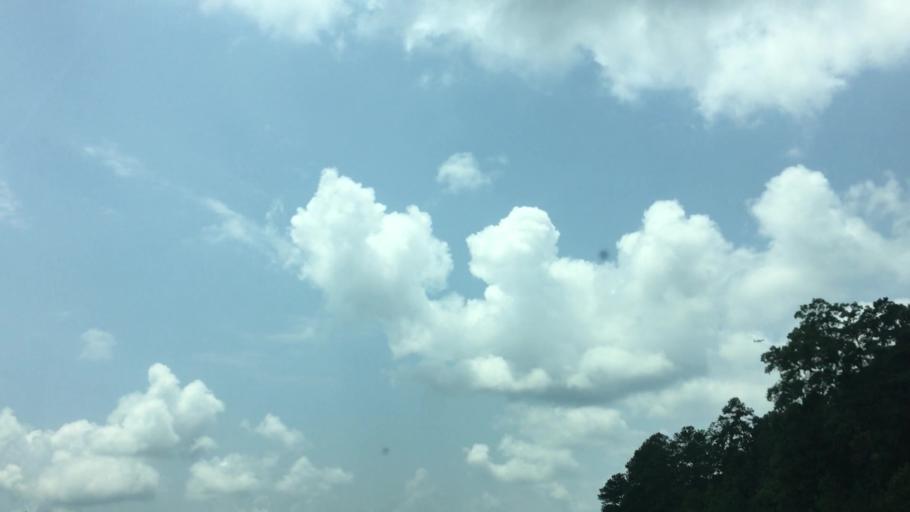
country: US
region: Georgia
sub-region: Fulton County
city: Palmetto
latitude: 33.5688
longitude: -84.6993
